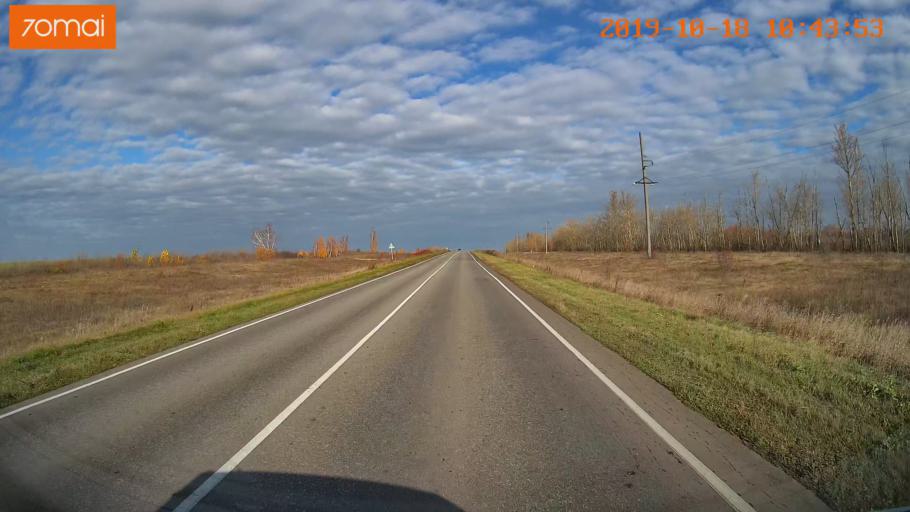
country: RU
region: Tula
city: Yepifan'
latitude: 53.6464
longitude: 38.6834
